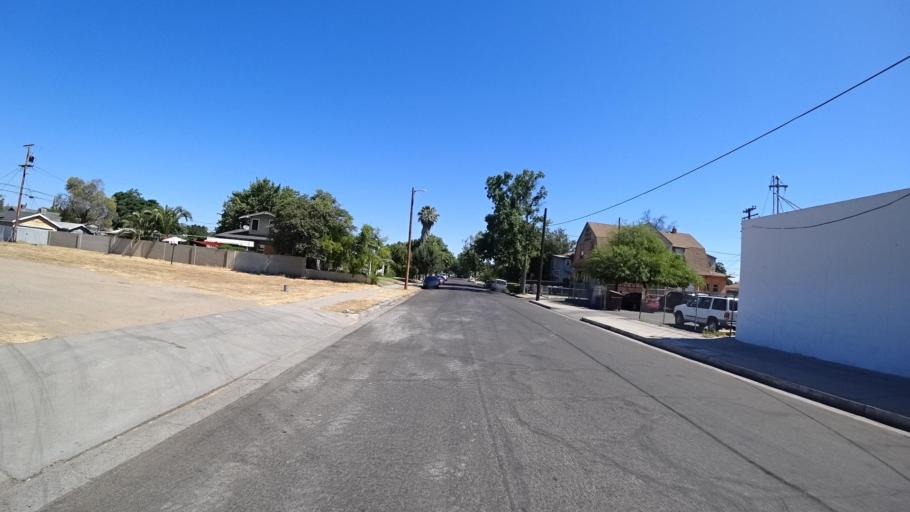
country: US
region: California
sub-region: Fresno County
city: Fresno
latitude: 36.7506
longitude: -119.8041
